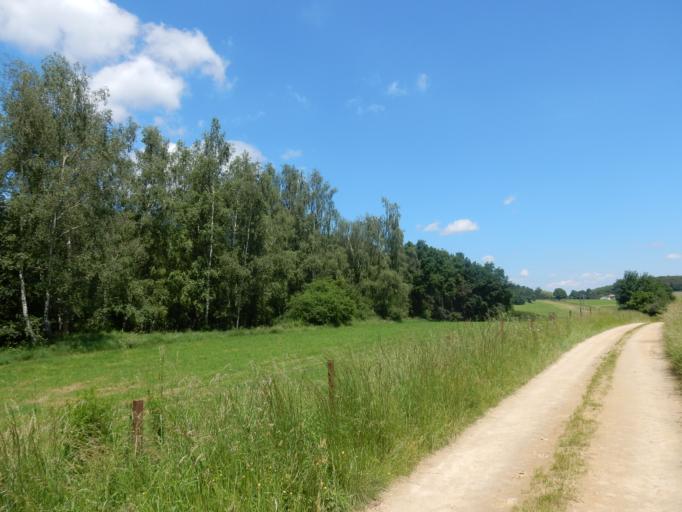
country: LU
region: Luxembourg
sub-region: Canton de Mersch
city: Boevange-sur-Attert
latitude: 49.7457
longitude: 6.0253
